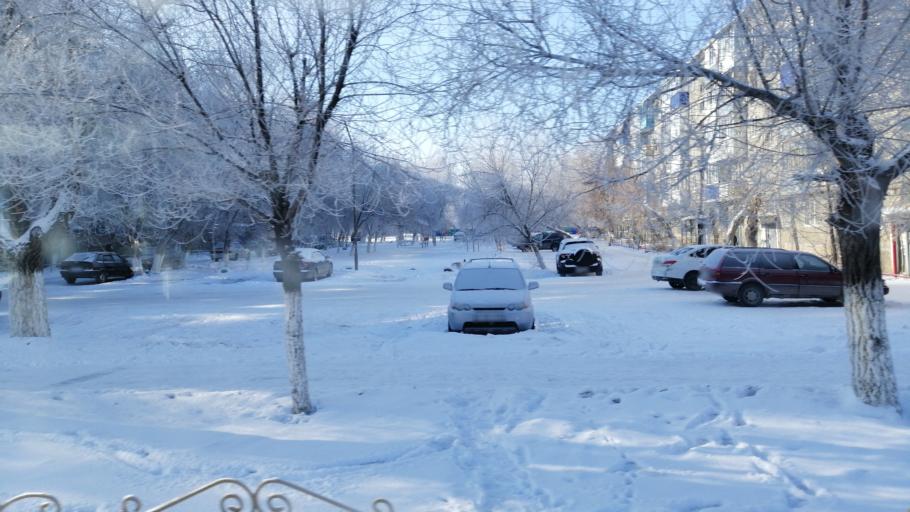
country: KZ
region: Aqtoebe
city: Aqtobe
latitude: 50.3045
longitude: 57.1514
